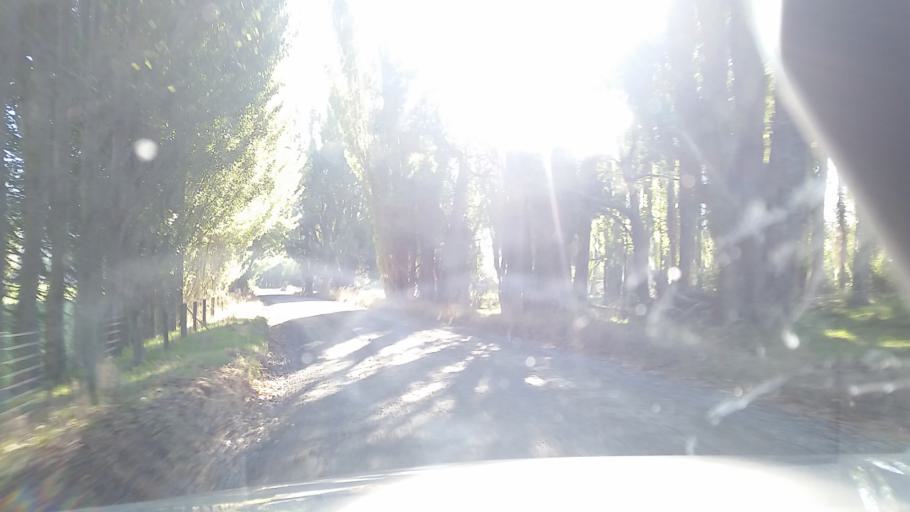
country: NZ
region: Marlborough
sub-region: Marlborough District
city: Blenheim
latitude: -41.4446
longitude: 173.8959
